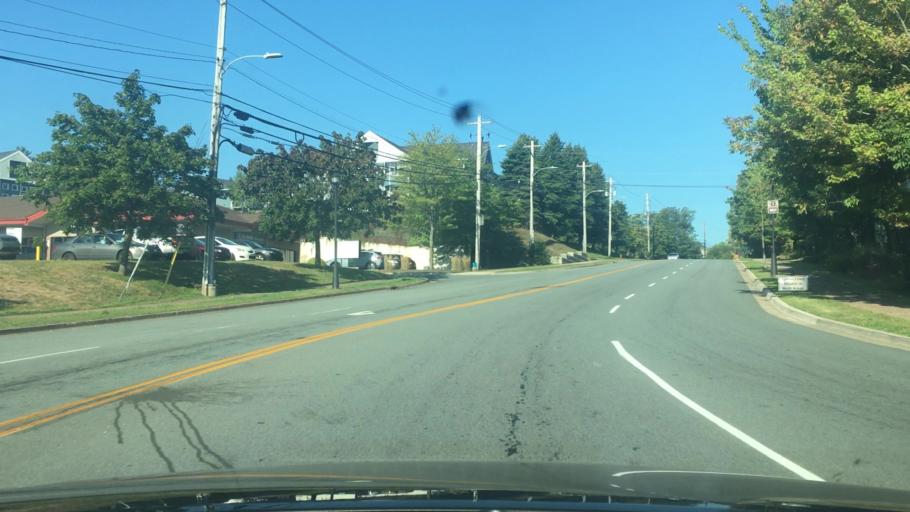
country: CA
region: Nova Scotia
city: Dartmouth
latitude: 44.7153
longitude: -63.6785
